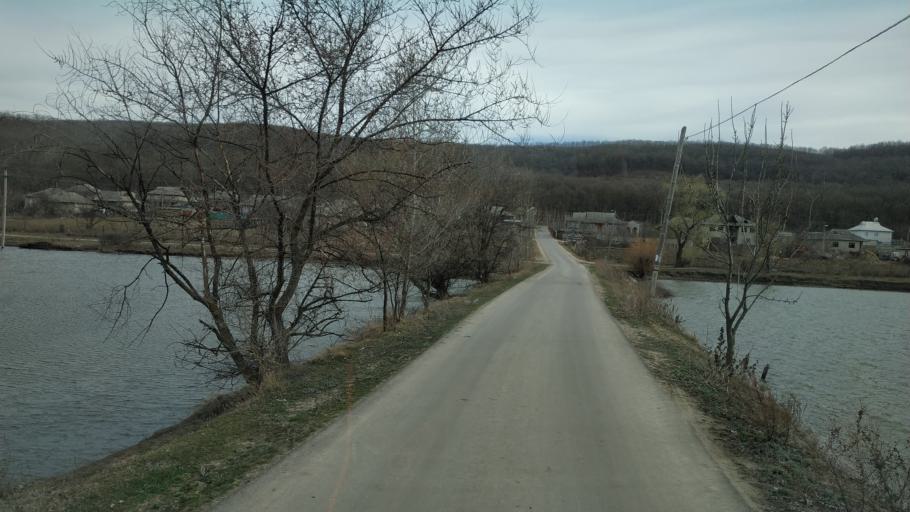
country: MD
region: Hincesti
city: Dancu
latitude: 46.8555
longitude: 28.2530
